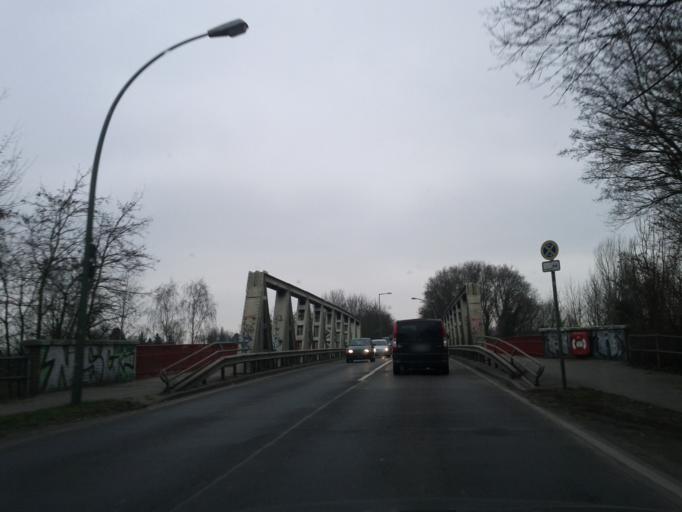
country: DE
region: Berlin
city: Baumschulenweg
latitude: 52.4592
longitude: 13.4793
